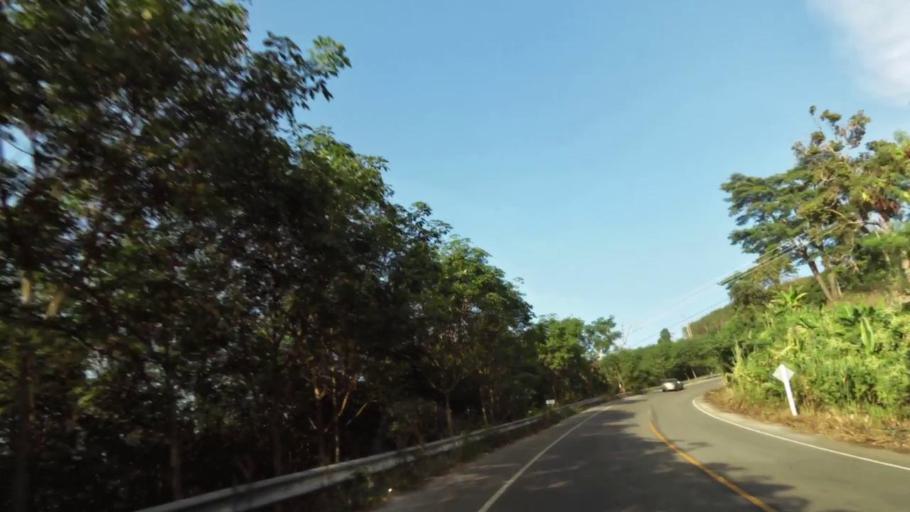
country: TH
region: Chiang Rai
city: Khun Tan
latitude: 19.8639
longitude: 100.4185
